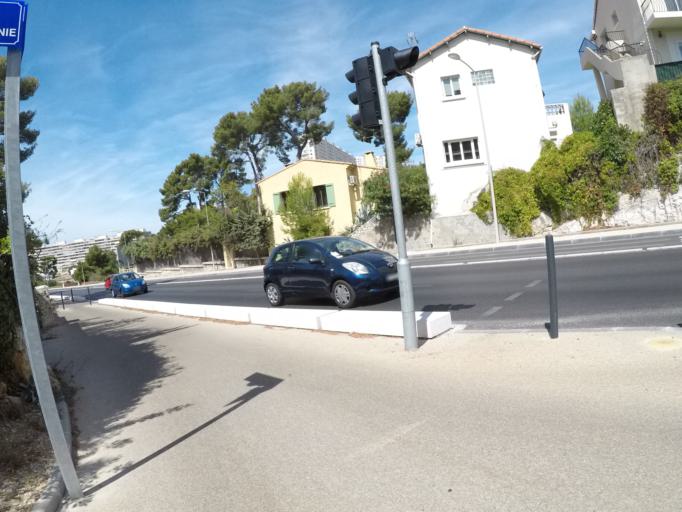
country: FR
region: Provence-Alpes-Cote d'Azur
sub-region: Departement des Bouches-du-Rhone
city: Marseille 09
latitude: 43.2458
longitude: 5.4209
